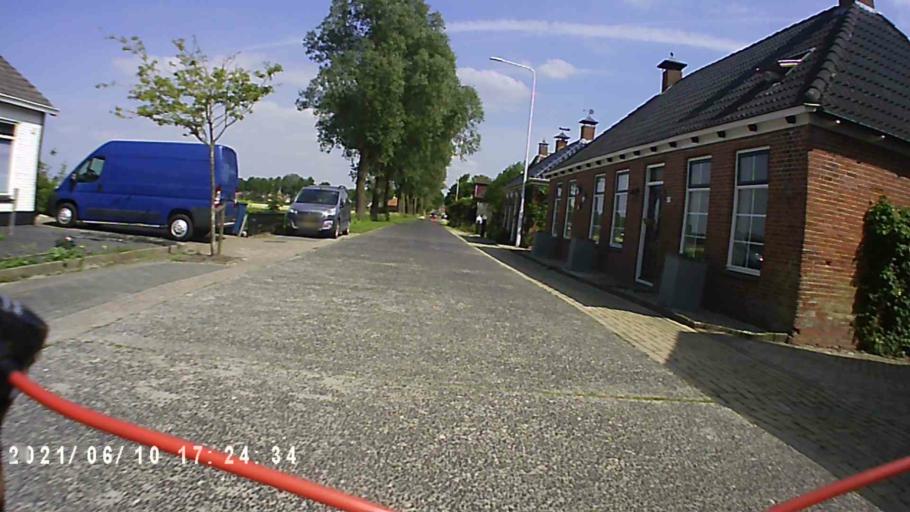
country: NL
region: Friesland
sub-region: Gemeente Kollumerland en Nieuwkruisland
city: Kollum
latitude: 53.2968
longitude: 6.2287
